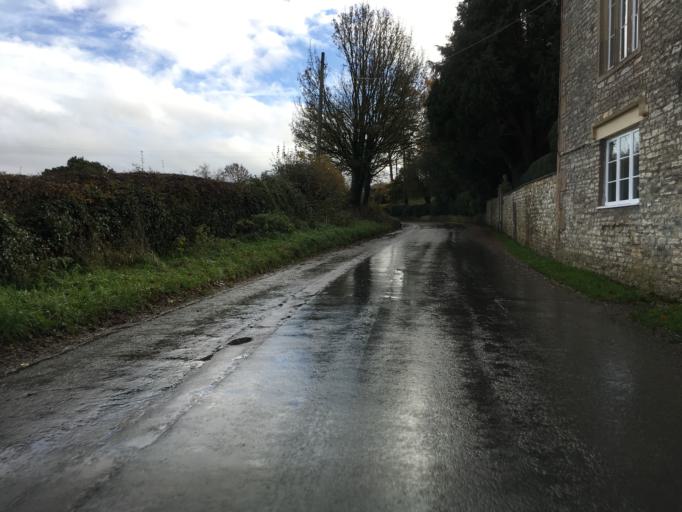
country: GB
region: England
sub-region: South Gloucestershire
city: Hinton
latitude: 51.4662
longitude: -2.4073
